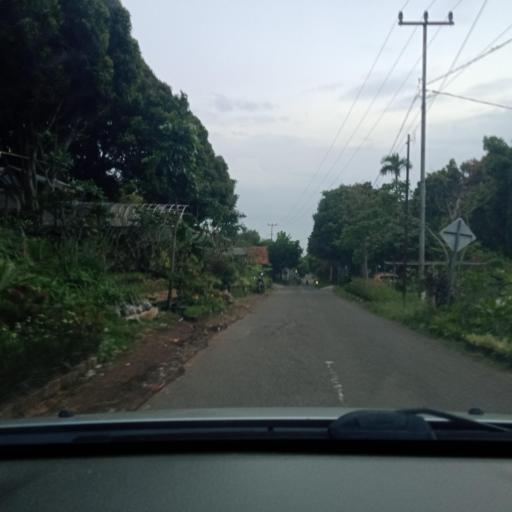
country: ID
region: West Java
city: Lembang
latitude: -6.8230
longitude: 107.5862
